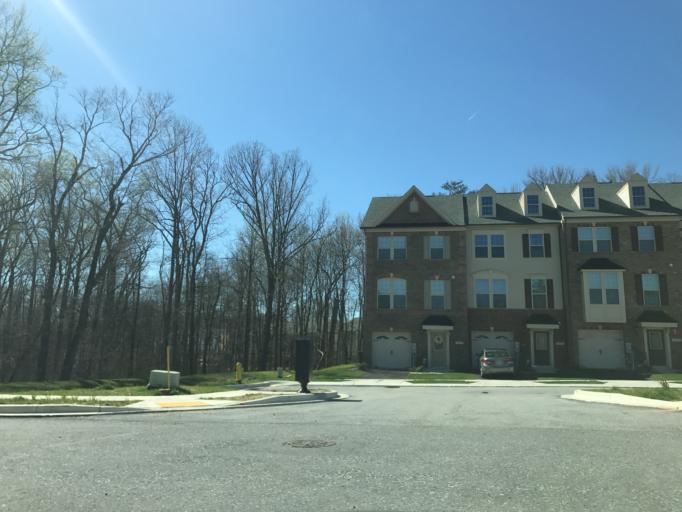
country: US
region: Maryland
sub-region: Anne Arundel County
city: Fort Meade
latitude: 39.1331
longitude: -76.7488
